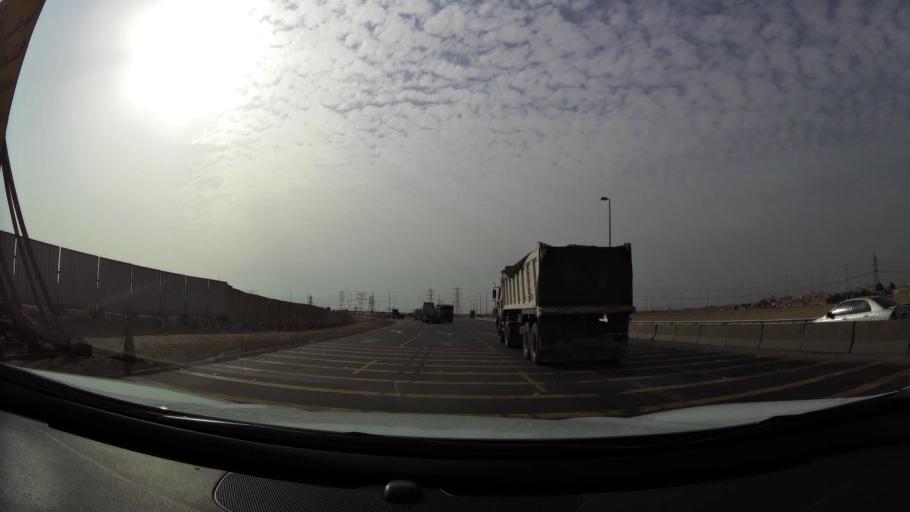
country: AE
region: Abu Dhabi
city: Abu Dhabi
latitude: 24.2933
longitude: 54.5518
